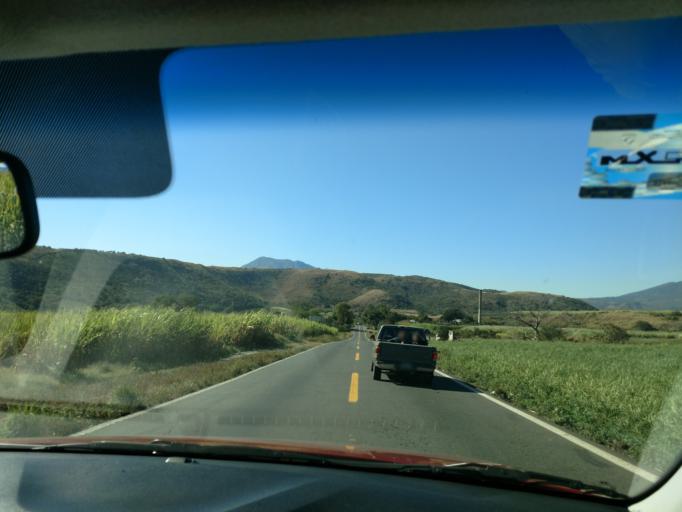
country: MX
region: Nayarit
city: San Pedro Lagunillas
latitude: 21.1520
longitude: -104.6172
